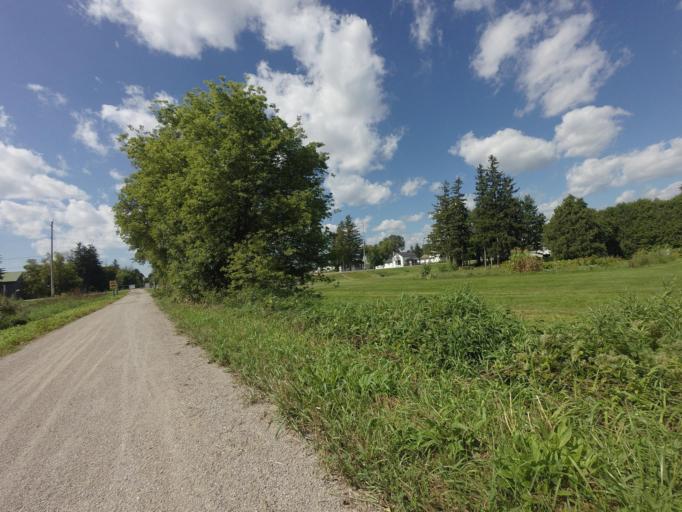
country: CA
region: Ontario
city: Huron East
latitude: 43.6800
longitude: -81.2991
